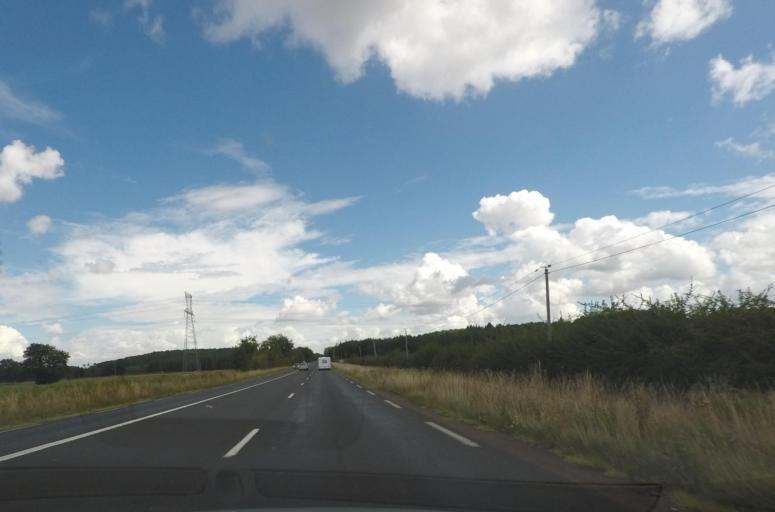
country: FR
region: Pays de la Loire
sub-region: Departement de la Sarthe
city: Cerans-Foulletourte
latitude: 47.8379
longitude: 0.0843
